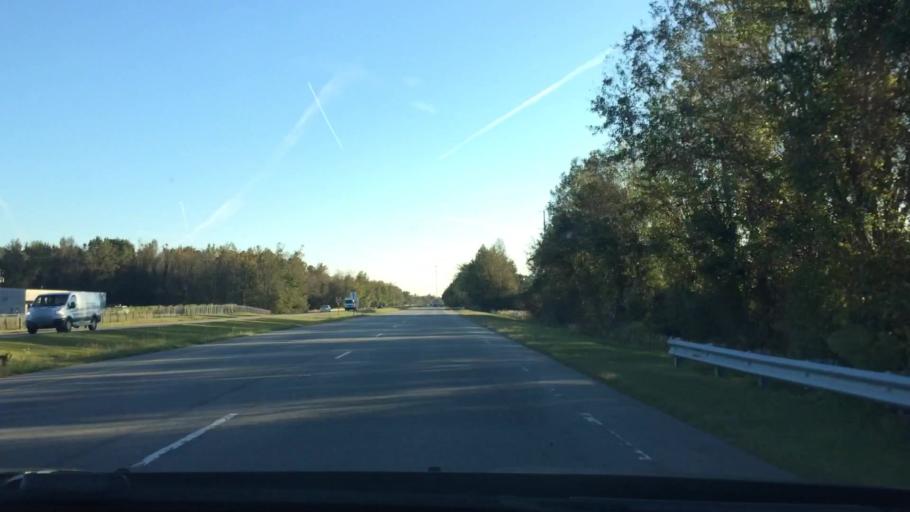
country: US
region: North Carolina
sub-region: Pitt County
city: Grifton
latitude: 35.3888
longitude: -77.4472
